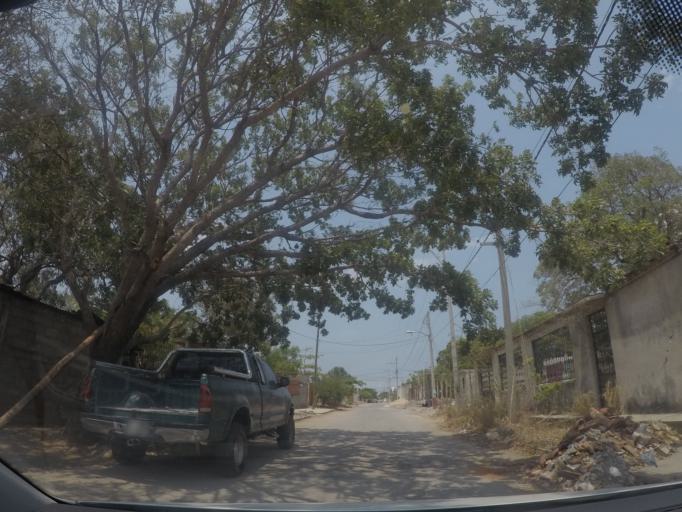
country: MX
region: Oaxaca
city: Asuncion Ixtaltepec
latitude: 16.5035
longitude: -95.0630
